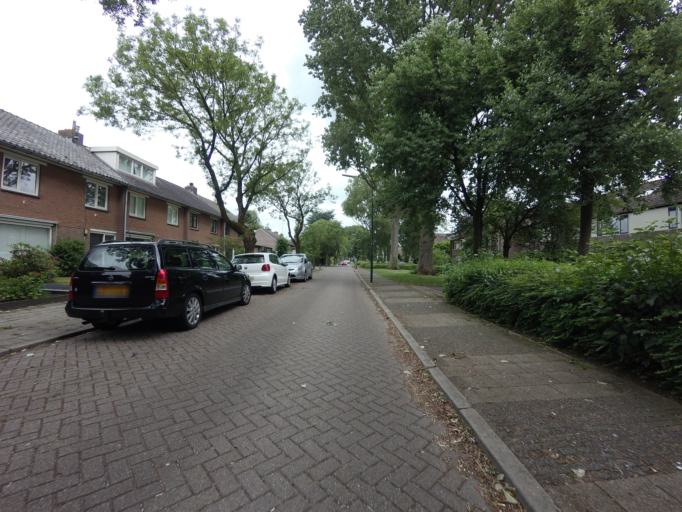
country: NL
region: Utrecht
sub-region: Gemeente Baarn
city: Baarn
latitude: 52.2018
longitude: 5.2999
